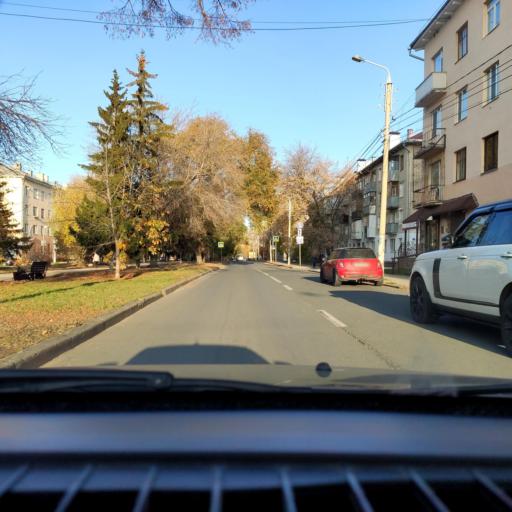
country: RU
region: Samara
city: Tol'yatti
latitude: 53.5146
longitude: 49.4120
